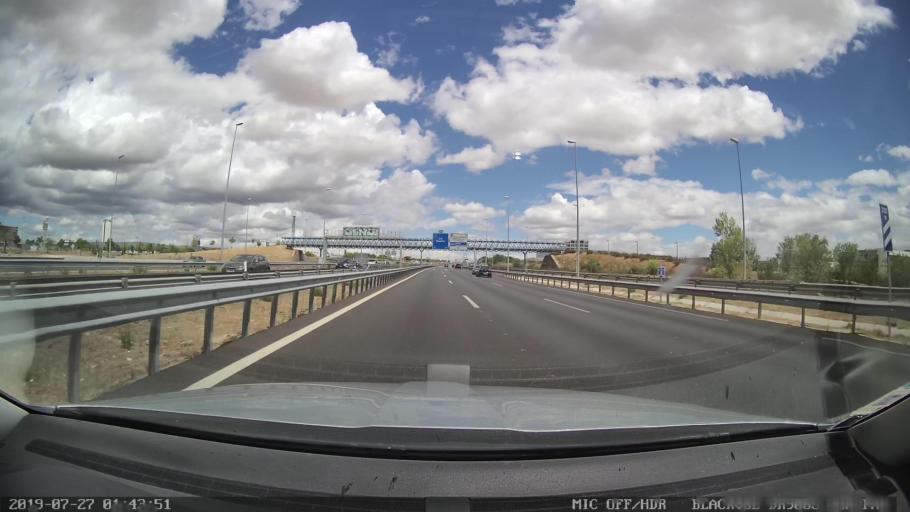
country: ES
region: Madrid
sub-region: Provincia de Madrid
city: Mostoles
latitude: 40.3362
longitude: -3.8806
